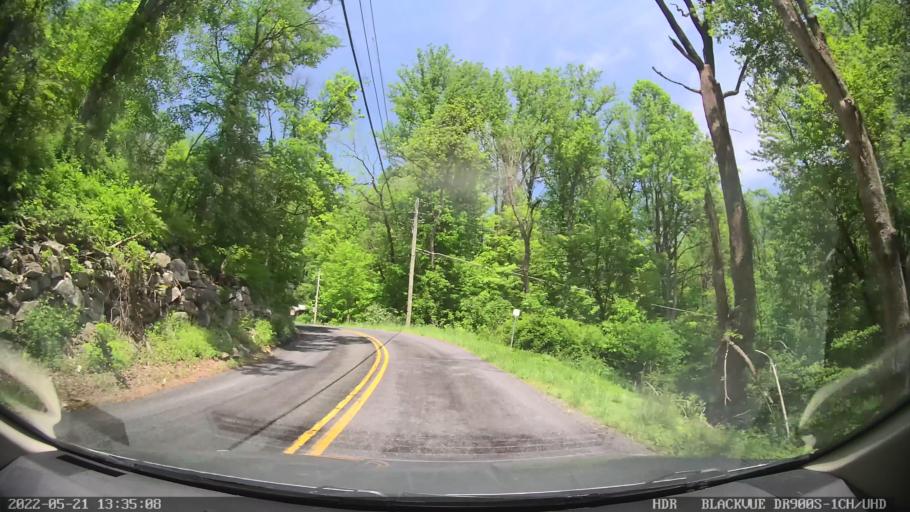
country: US
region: Pennsylvania
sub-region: Berks County
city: Topton
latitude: 40.4469
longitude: -75.6776
